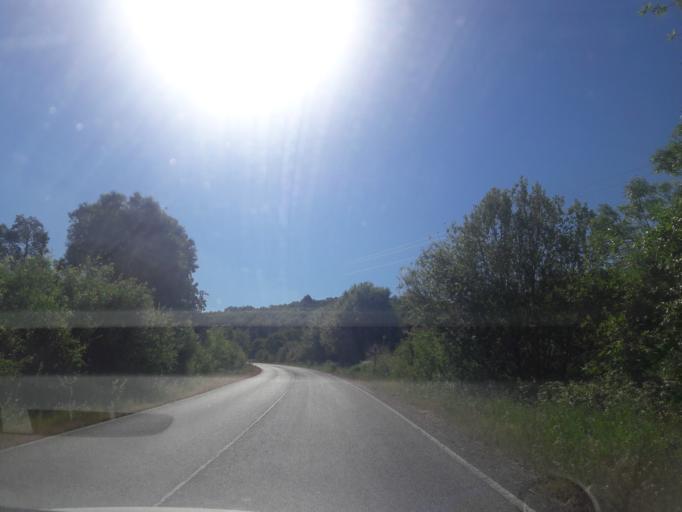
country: ES
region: Castille and Leon
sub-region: Provincia de Salamanca
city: Penacaballera
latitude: 40.3428
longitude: -5.8614
